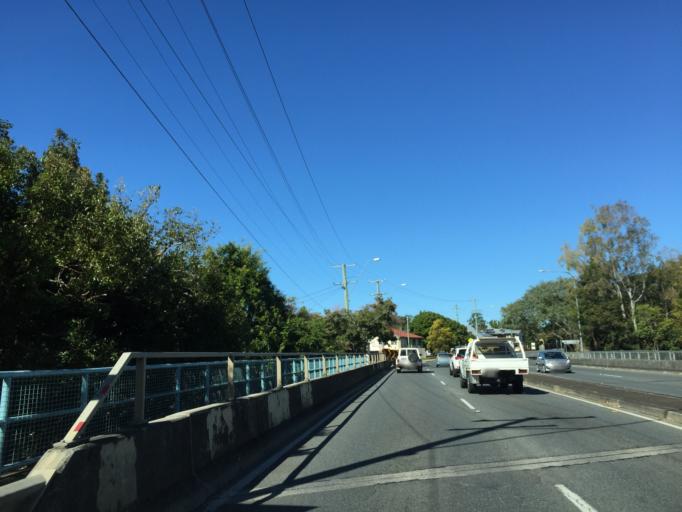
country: AU
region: Queensland
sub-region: Brisbane
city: Everton Park
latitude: -27.4122
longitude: 152.9924
